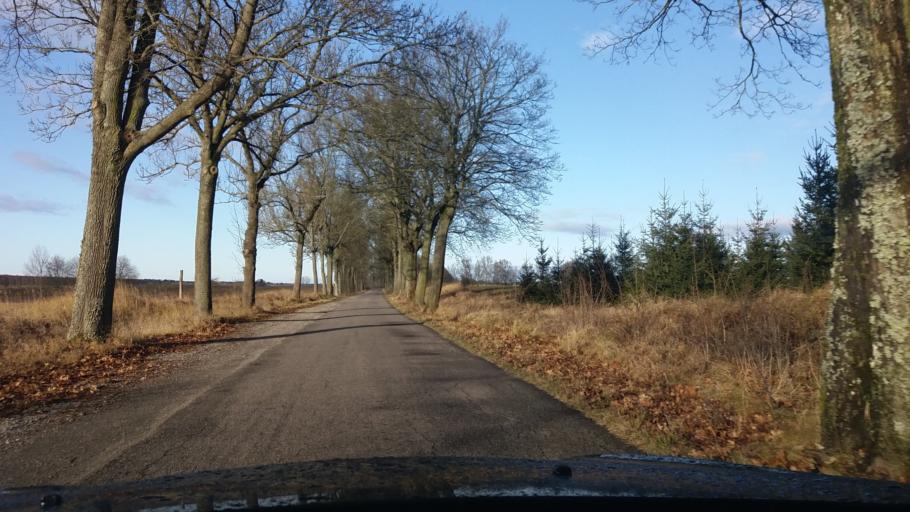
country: PL
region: West Pomeranian Voivodeship
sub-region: Powiat choszczenski
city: Drawno
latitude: 53.1823
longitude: 15.8019
